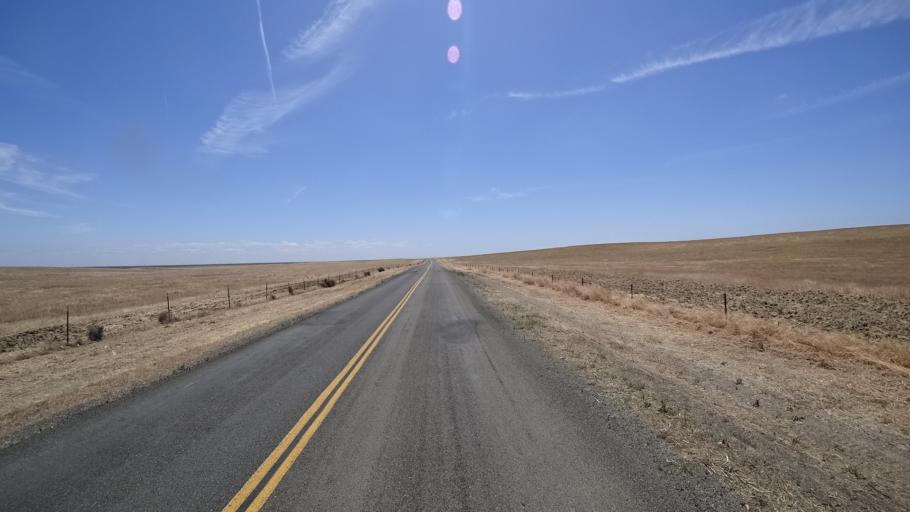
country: US
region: California
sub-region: Kings County
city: Kettleman City
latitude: 35.8165
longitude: -119.9038
